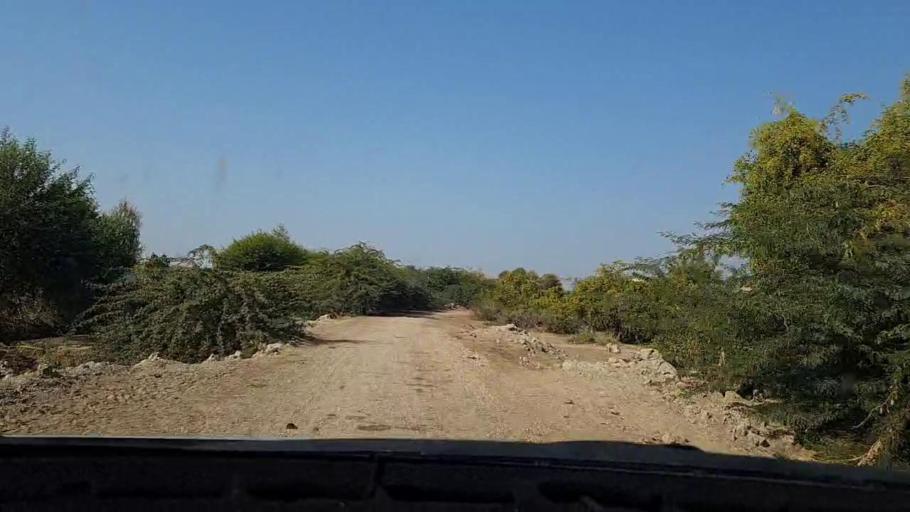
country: PK
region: Sindh
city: Tando Mittha Khan
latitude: 25.8309
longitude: 69.2875
